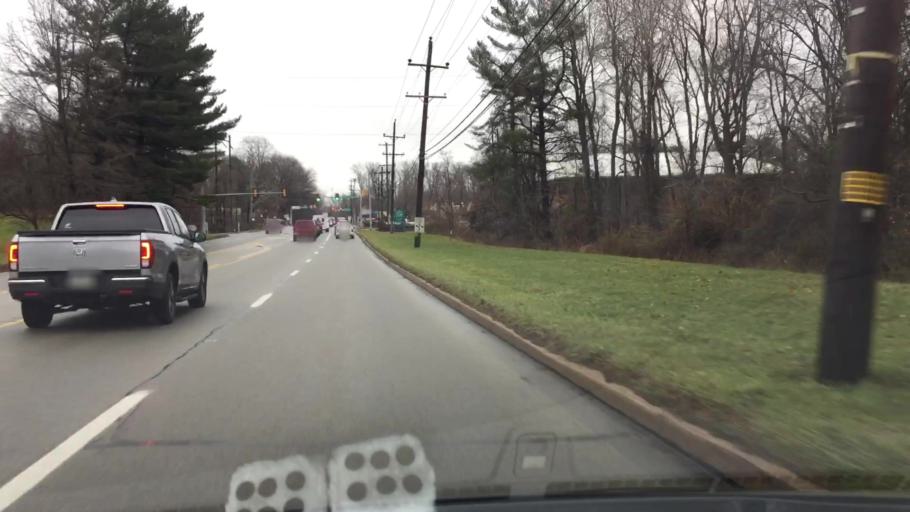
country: US
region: Pennsylvania
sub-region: Delaware County
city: Lima
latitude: 39.9068
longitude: -75.4169
